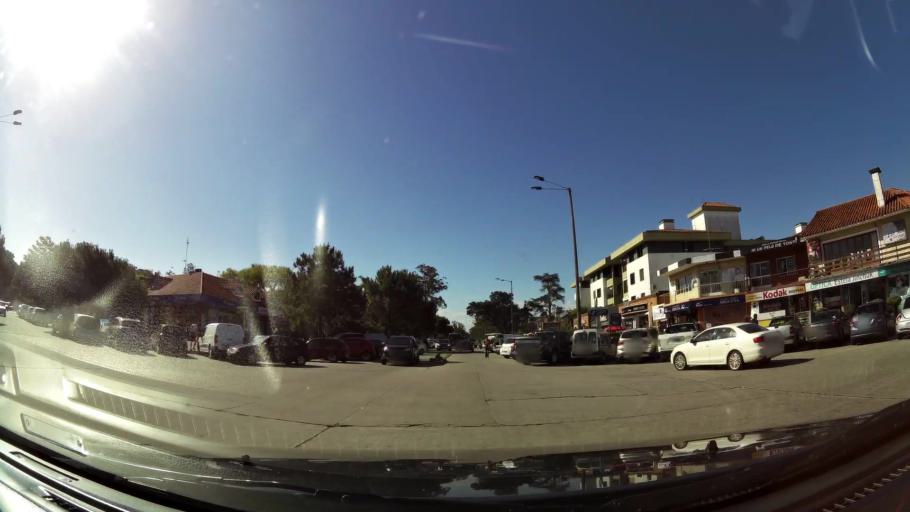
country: UY
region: Canelones
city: Paso de Carrasco
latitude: -34.8876
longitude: -56.0579
